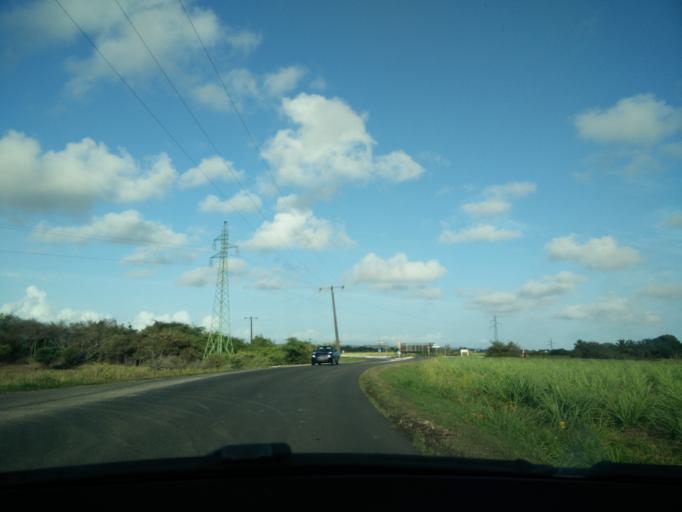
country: GP
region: Guadeloupe
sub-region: Guadeloupe
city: Le Moule
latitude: 16.3144
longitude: -61.3632
